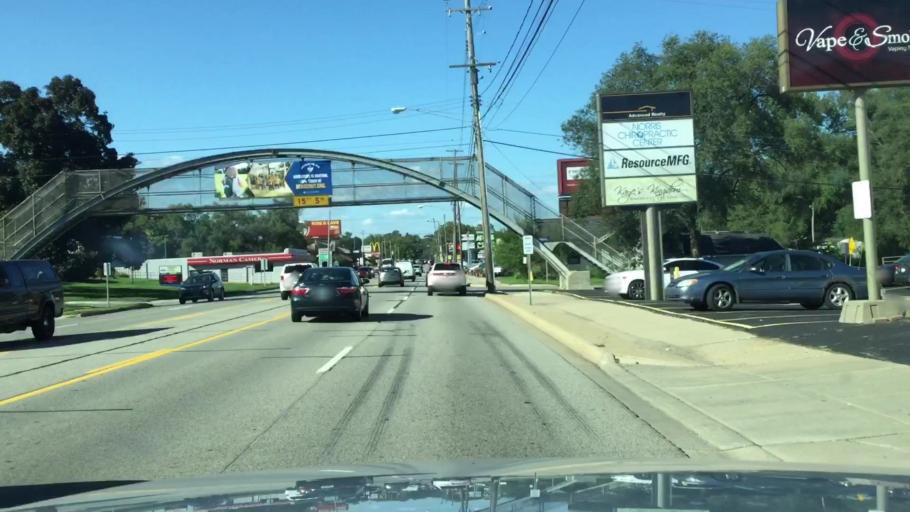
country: US
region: Michigan
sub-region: Kalamazoo County
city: Kalamazoo
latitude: 42.2543
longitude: -85.5896
